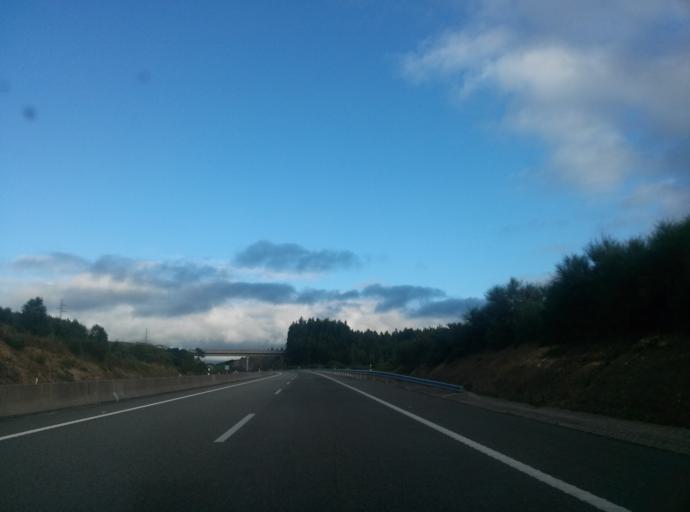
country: ES
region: Galicia
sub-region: Provincia de Lugo
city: Vilalba
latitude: 43.3490
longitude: -7.7348
